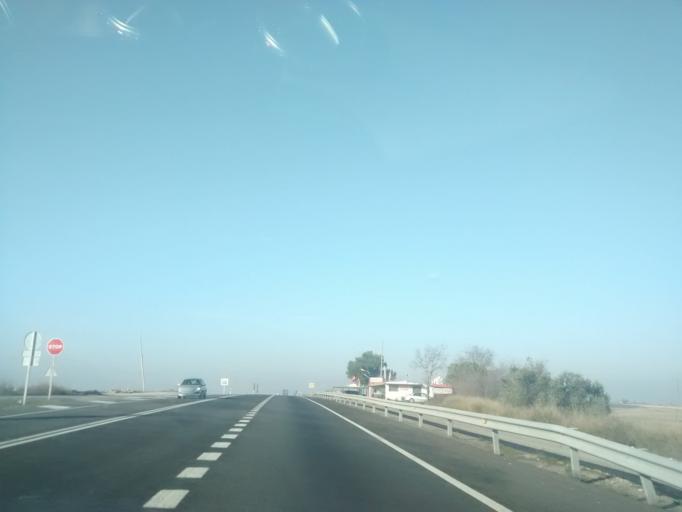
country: ES
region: Aragon
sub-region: Provincia de Huesca
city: Fraga
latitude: 41.5142
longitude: 0.2708
